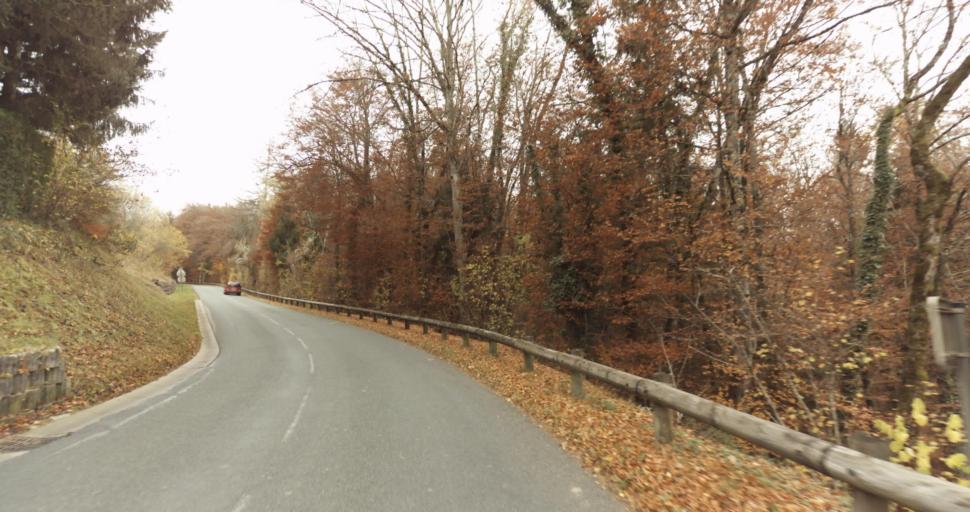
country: FR
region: Rhone-Alpes
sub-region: Departement de la Haute-Savoie
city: Saint-Martin-Bellevue
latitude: 45.9690
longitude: 6.1497
